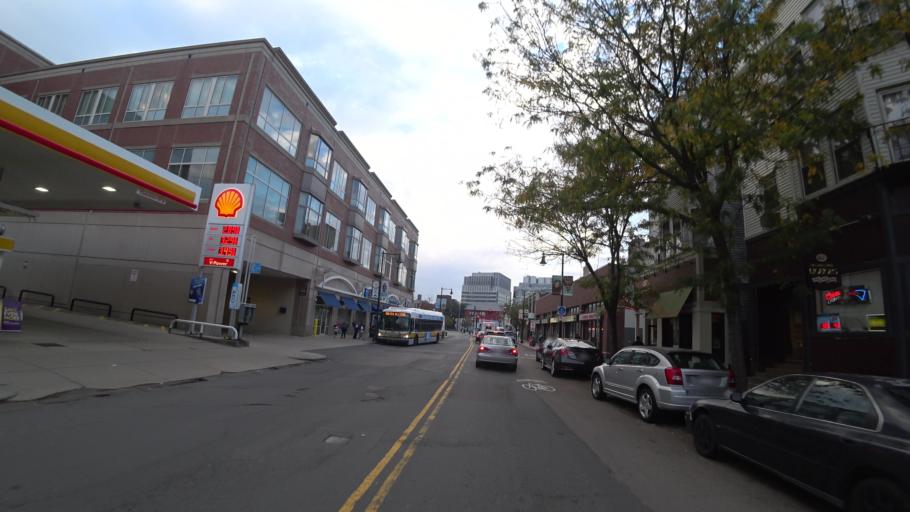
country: US
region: Massachusetts
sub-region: Norfolk County
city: Brookline
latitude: 42.3337
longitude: -71.1034
